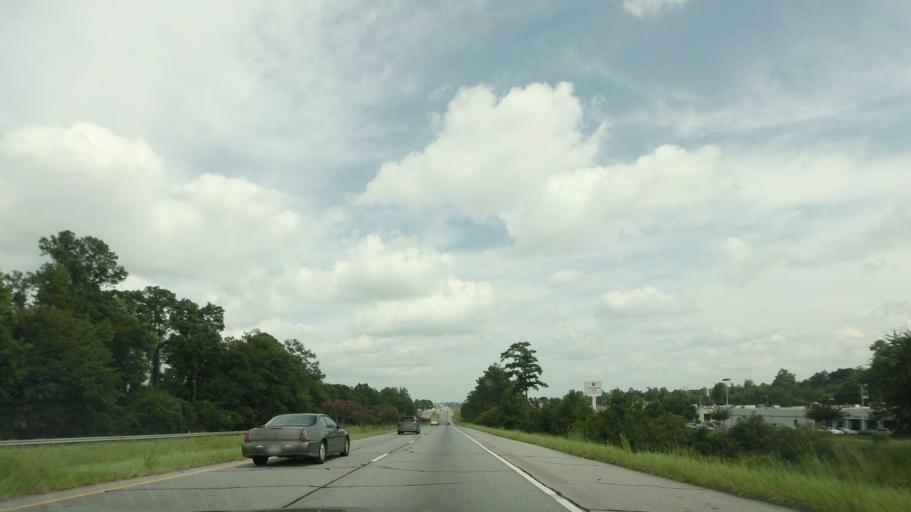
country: US
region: Georgia
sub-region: Bibb County
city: Macon
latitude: 32.8162
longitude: -83.7051
